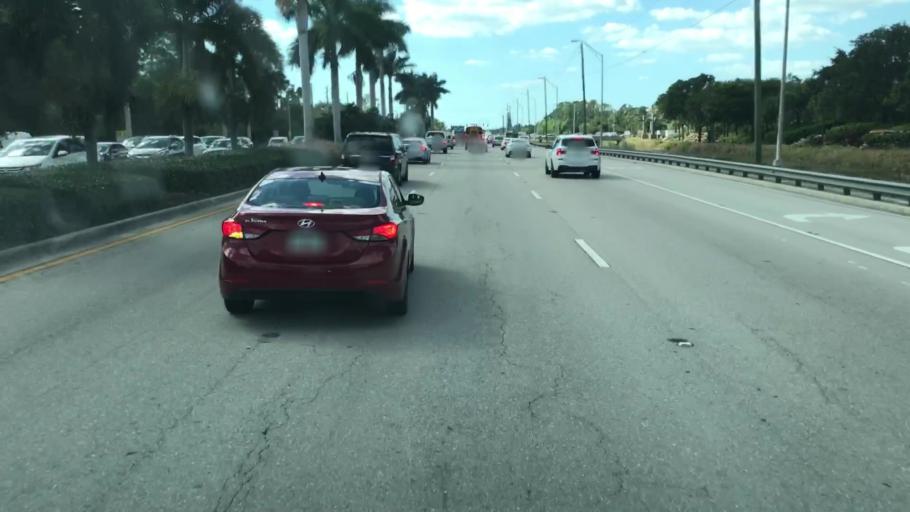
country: US
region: Florida
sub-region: Collier County
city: Naples Park
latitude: 26.2728
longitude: -81.7498
